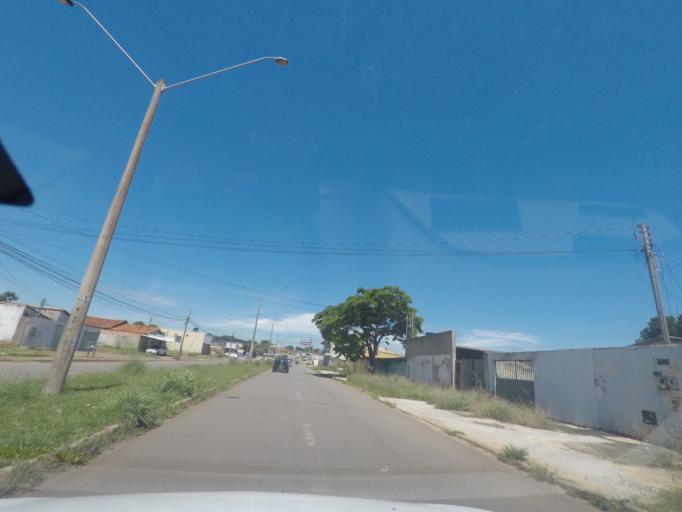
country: BR
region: Goias
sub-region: Aparecida De Goiania
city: Aparecida de Goiania
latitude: -16.7707
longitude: -49.3285
